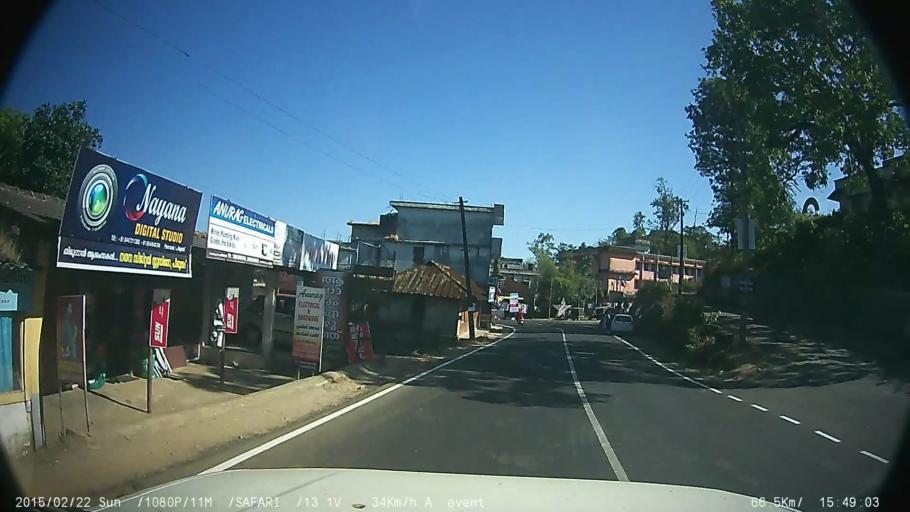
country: IN
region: Kerala
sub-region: Kottayam
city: Erattupetta
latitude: 9.5724
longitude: 76.9955
